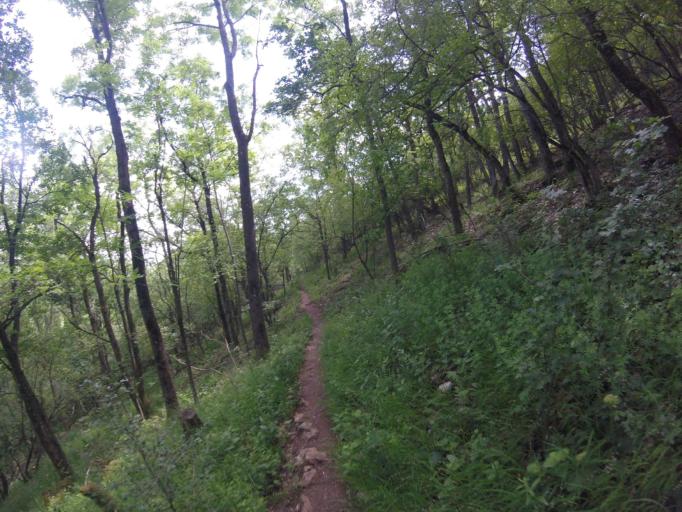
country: SK
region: Kosicky
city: Medzev
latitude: 48.6175
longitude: 20.8608
